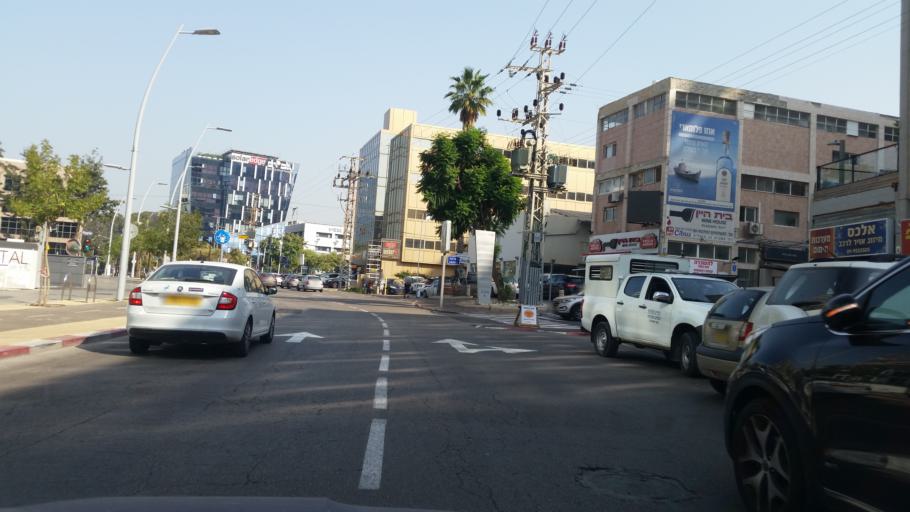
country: IL
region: Tel Aviv
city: Herzliya Pituah
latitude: 32.1648
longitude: 34.8114
